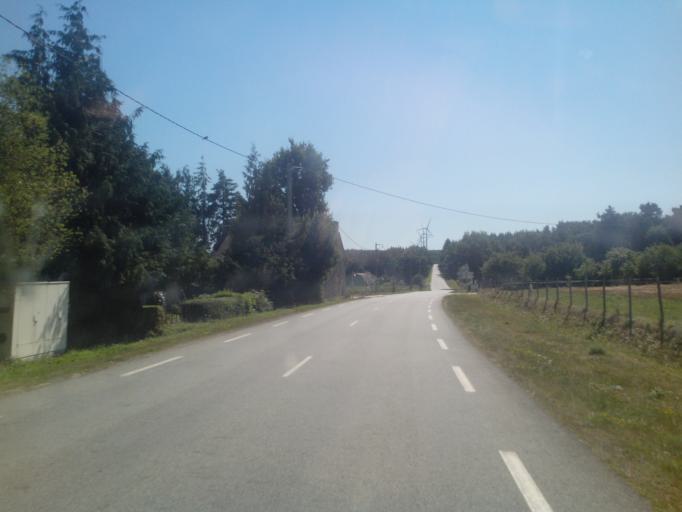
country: FR
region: Brittany
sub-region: Departement du Morbihan
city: Guegon
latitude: 47.9172
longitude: -2.5247
